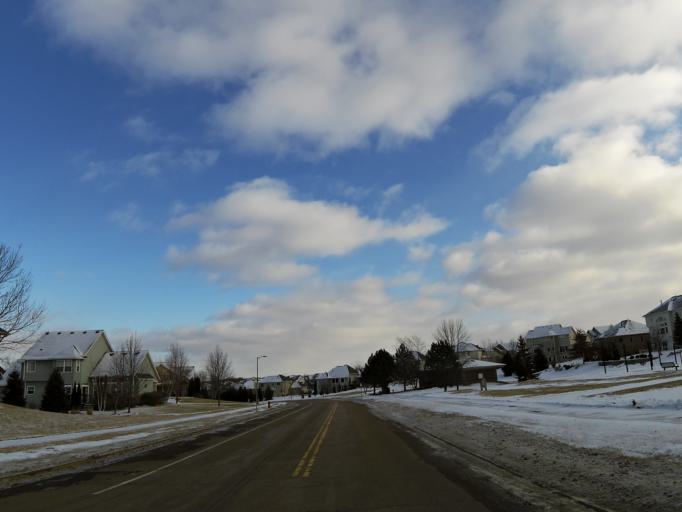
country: US
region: Minnesota
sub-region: Scott County
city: Prior Lake
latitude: 44.7293
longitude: -93.4577
